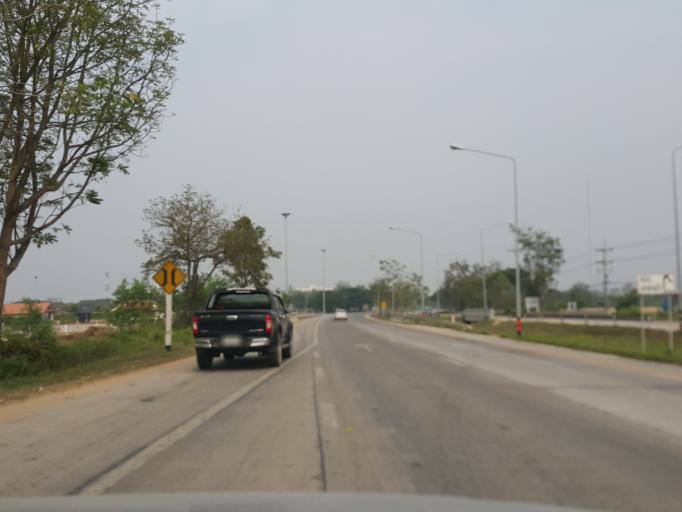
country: TH
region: Lampang
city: Ko Kha
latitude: 18.1917
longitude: 99.4065
